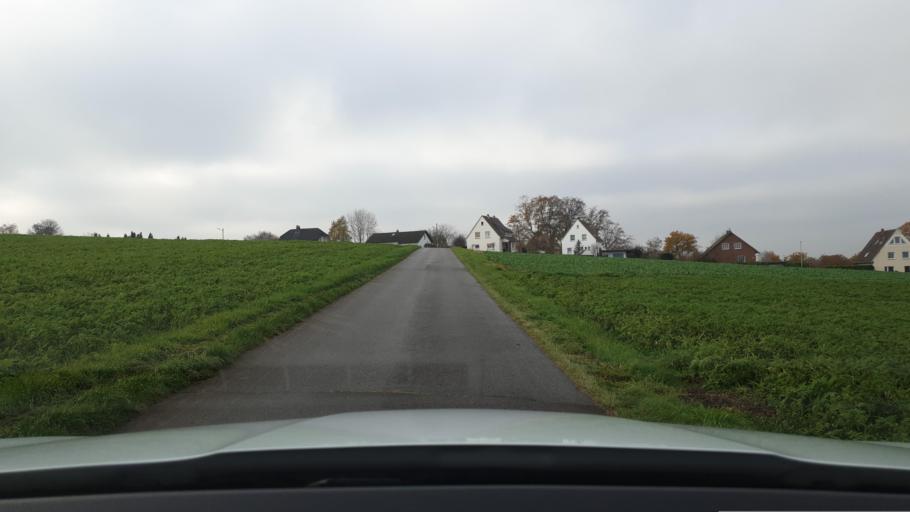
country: DE
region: North Rhine-Westphalia
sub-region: Regierungsbezirk Detmold
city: Vlotho
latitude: 52.1968
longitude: 8.8422
